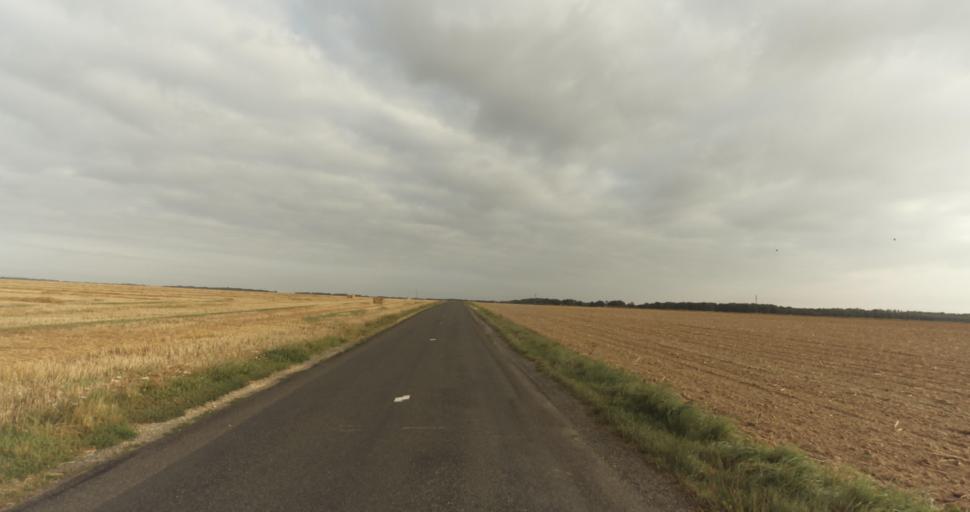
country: FR
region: Centre
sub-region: Departement d'Eure-et-Loir
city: Vert-en-Drouais
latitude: 48.7789
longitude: 1.2970
